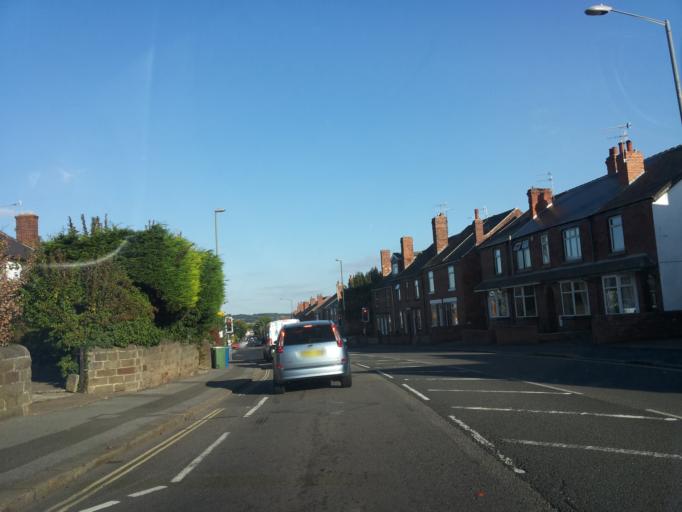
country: GB
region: England
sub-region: Derbyshire
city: Wingerworth
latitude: 53.2308
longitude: -1.4690
